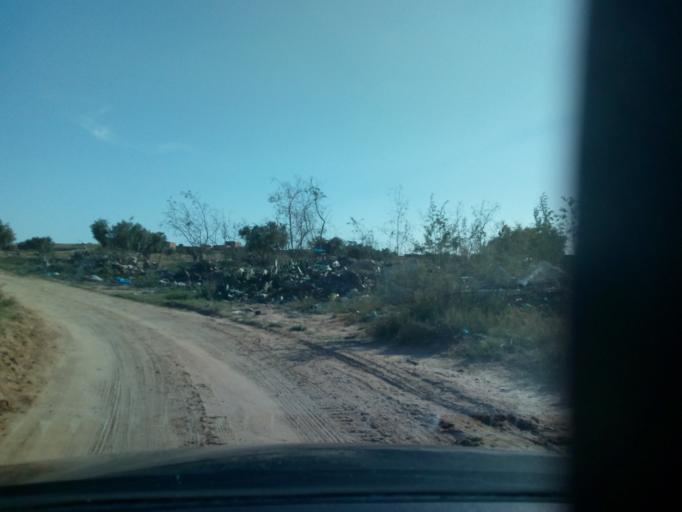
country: TN
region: Safaqis
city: Sfax
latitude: 34.7258
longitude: 10.6127
